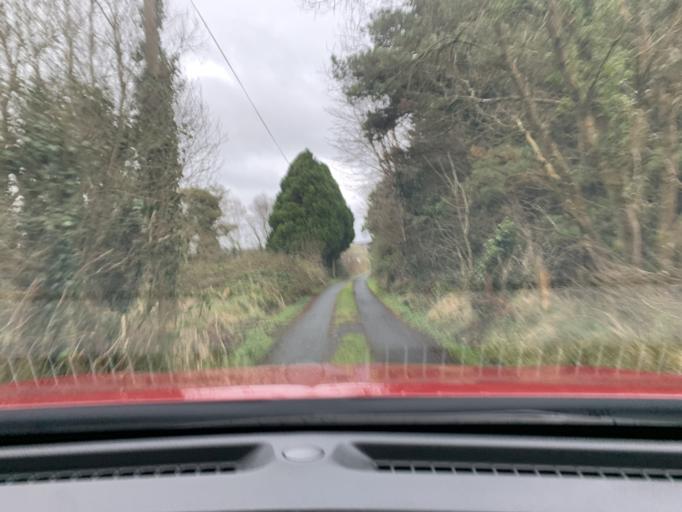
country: IE
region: Connaught
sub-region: Roscommon
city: Ballaghaderreen
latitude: 53.9647
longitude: -8.5056
